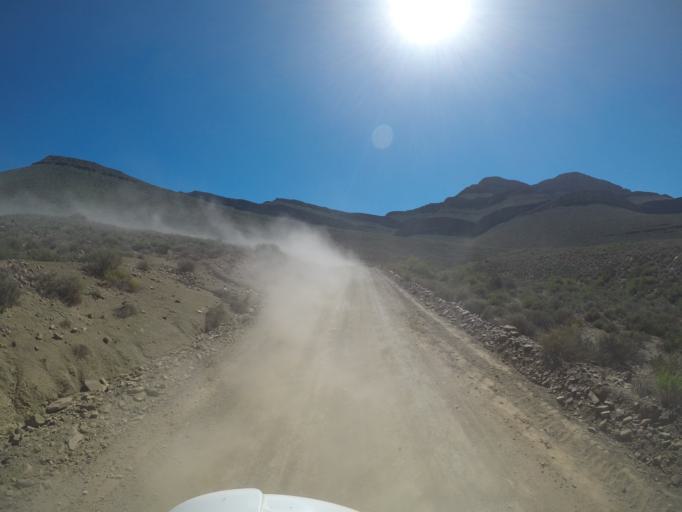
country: ZA
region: Western Cape
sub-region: West Coast District Municipality
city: Clanwilliam
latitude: -32.6196
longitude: 19.3841
